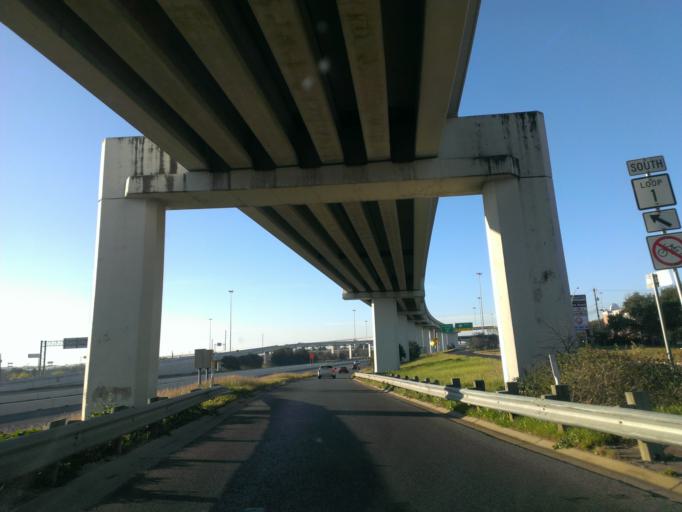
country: US
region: Texas
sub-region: Williamson County
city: Jollyville
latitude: 30.3849
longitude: -97.7362
